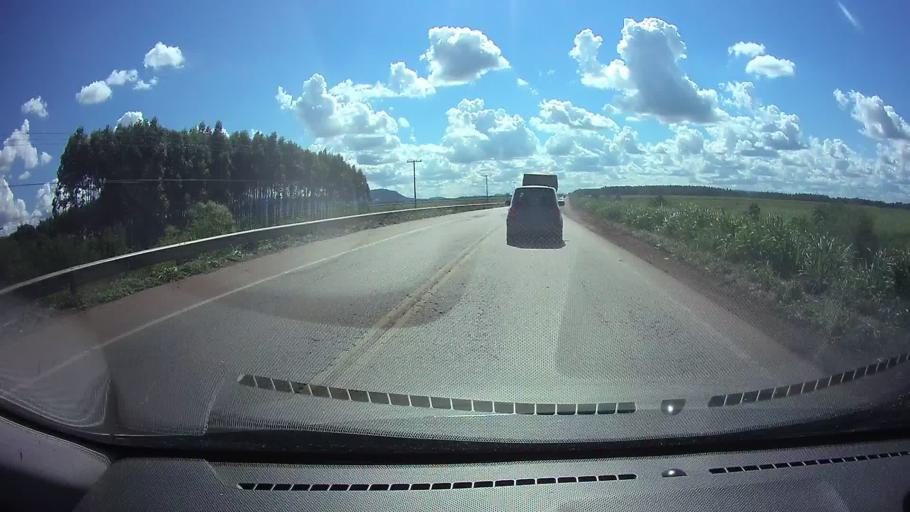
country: PY
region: Guaira
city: Coronel Martinez
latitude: -25.7644
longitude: -56.7305
